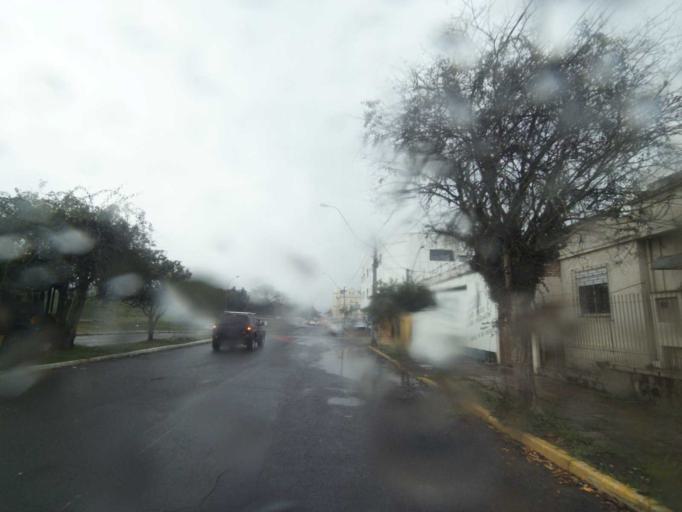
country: BR
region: Rio Grande do Sul
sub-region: Sao Leopoldo
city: Sao Leopoldo
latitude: -29.7613
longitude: -51.1511
